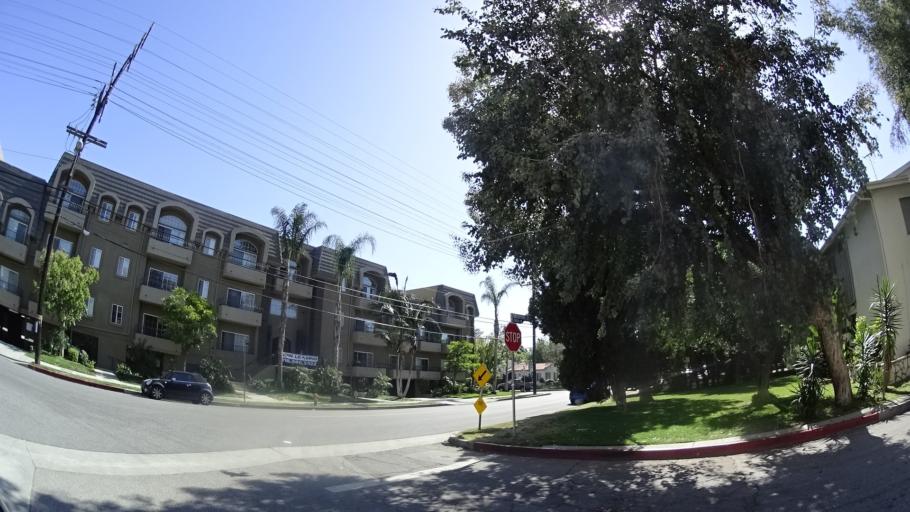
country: US
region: California
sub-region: Los Angeles County
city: Universal City
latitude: 34.1504
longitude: -118.3630
